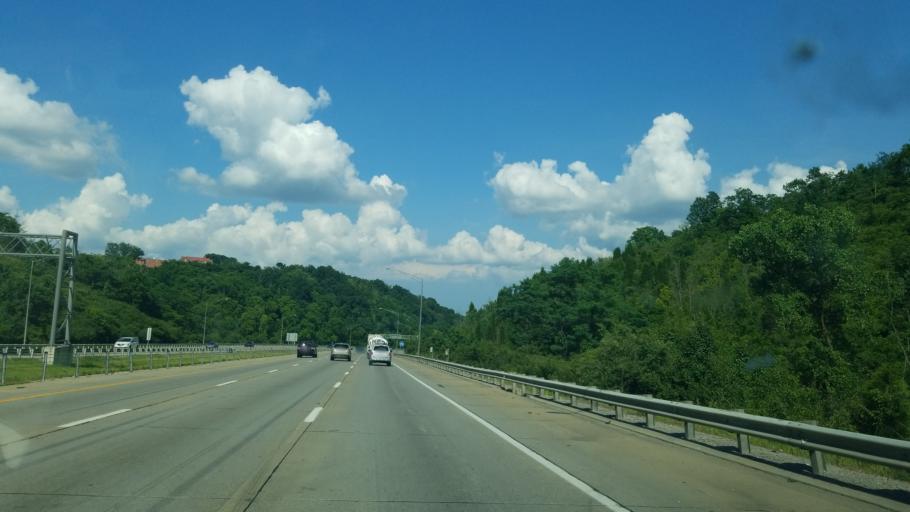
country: US
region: Kentucky
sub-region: Kenton County
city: Lakeside Park
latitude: 39.0258
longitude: -84.5575
